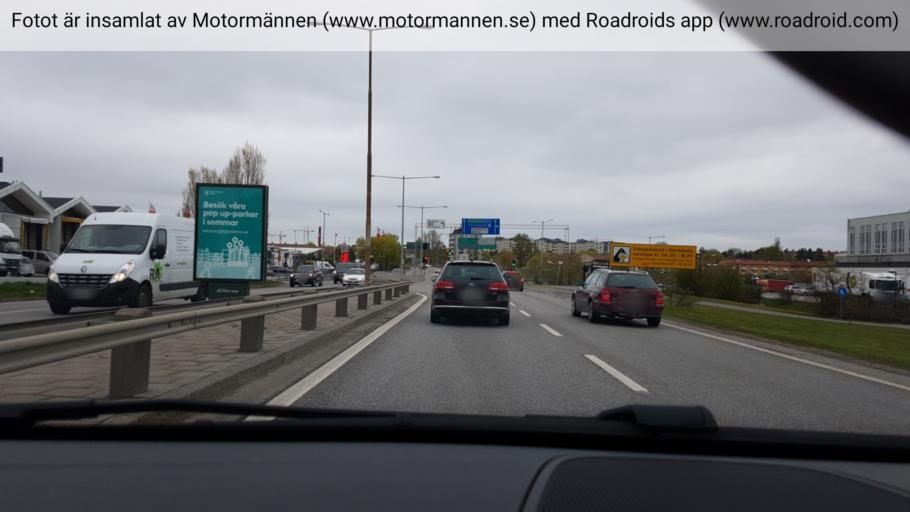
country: SE
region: Stockholm
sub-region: Stockholms Kommun
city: Arsta
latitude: 59.2936
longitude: 18.0341
